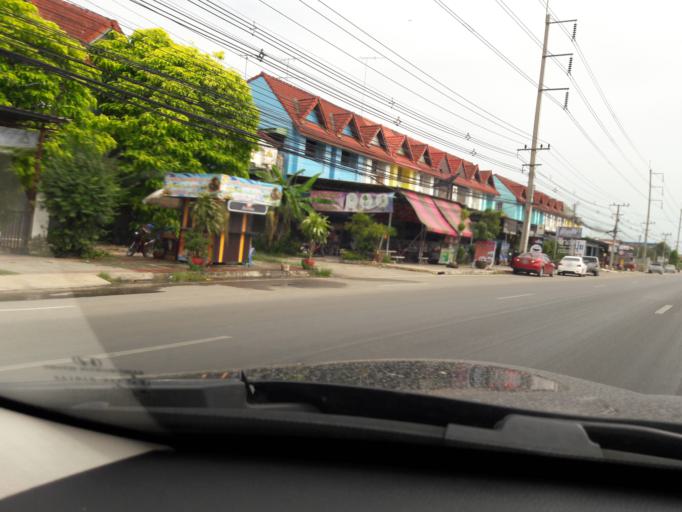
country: TH
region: Ratchaburi
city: Damnoen Saduak
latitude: 13.5576
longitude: 99.9684
